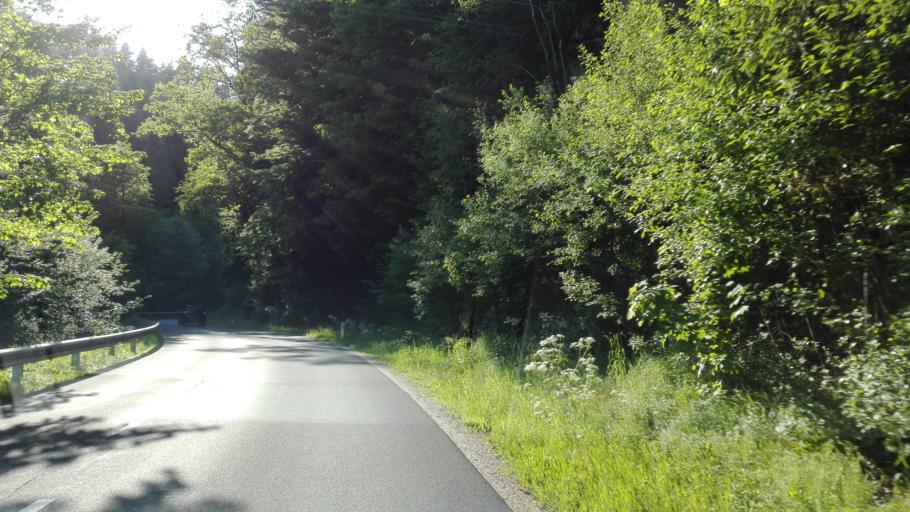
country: AT
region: Upper Austria
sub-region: Politischer Bezirk Perg
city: Perg
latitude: 48.4148
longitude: 14.6402
